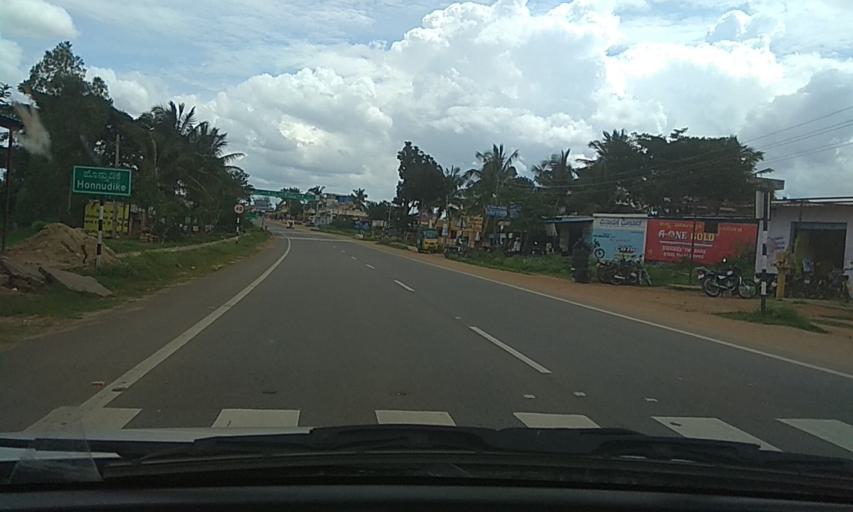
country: IN
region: Karnataka
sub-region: Tumkur
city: Tumkur
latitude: 13.2653
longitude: 77.0876
